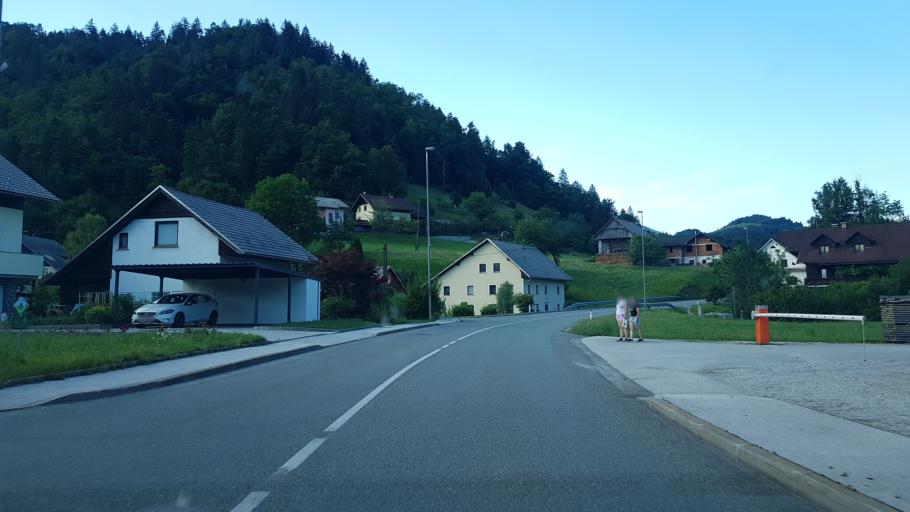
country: SI
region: Gorenja Vas-Poljane
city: Gorenja Vas
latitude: 46.1021
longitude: 14.1111
